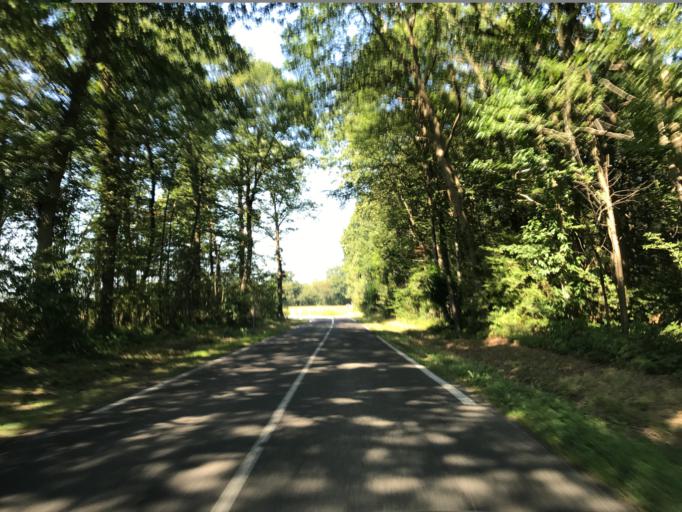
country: FR
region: Haute-Normandie
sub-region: Departement de l'Eure
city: Houlbec-Cocherel
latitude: 49.0941
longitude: 1.3510
